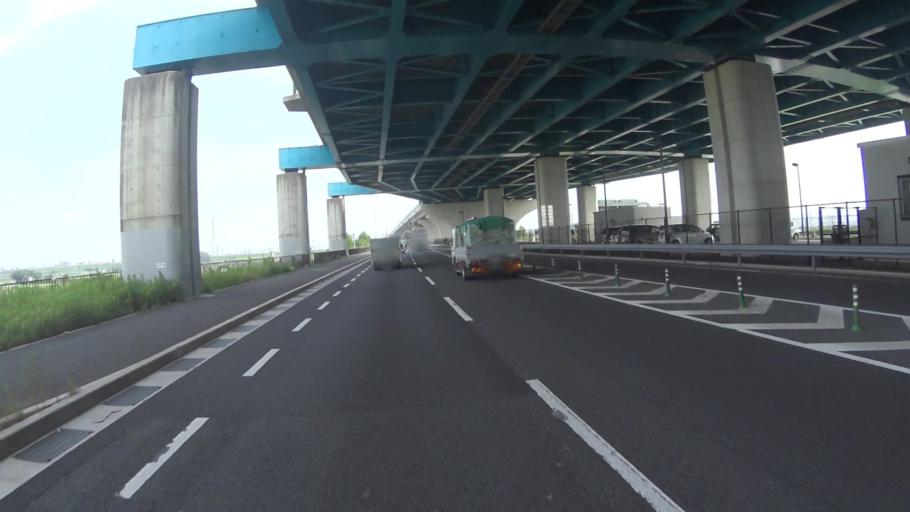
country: JP
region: Kyoto
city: Uji
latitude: 34.9092
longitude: 135.7494
